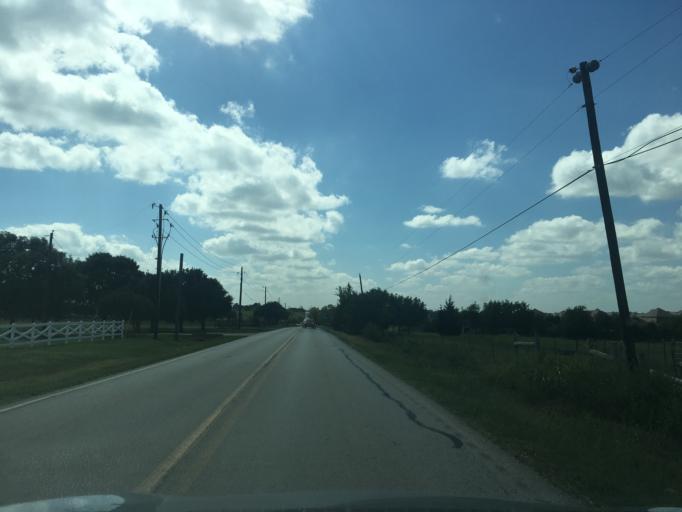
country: US
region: Texas
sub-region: Dallas County
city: Sachse
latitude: 32.9679
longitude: -96.5704
